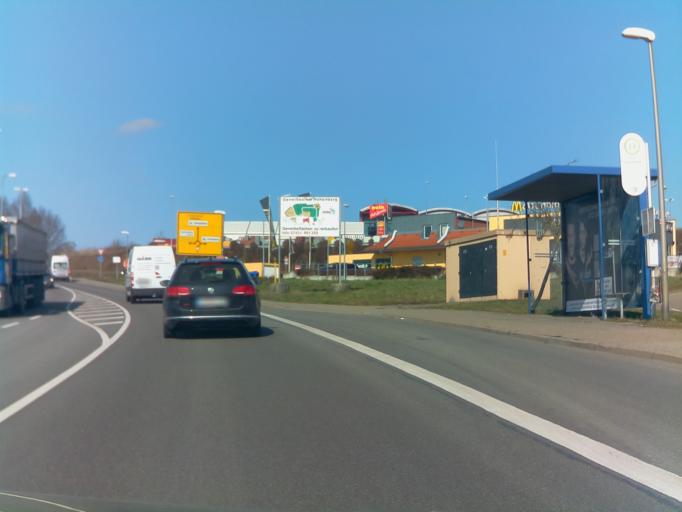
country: DE
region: Baden-Wuerttemberg
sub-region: Karlsruhe Region
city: Horb am Neckar
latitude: 48.4573
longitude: 8.6970
